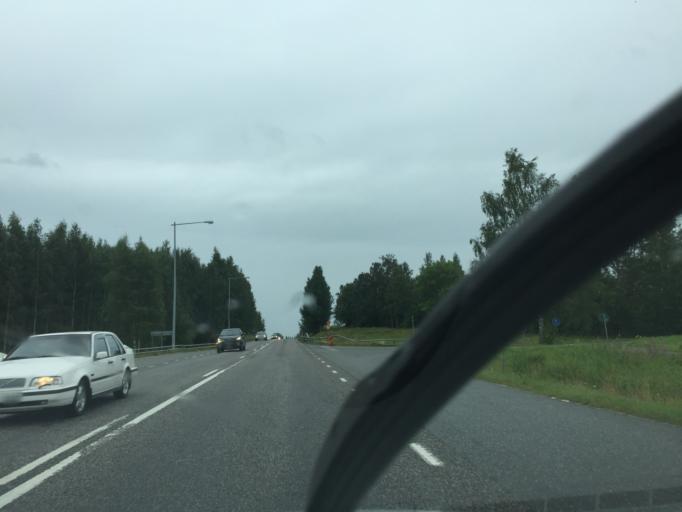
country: SE
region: OErebro
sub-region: Kumla Kommun
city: Hallabrottet
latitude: 59.1873
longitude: 15.2511
